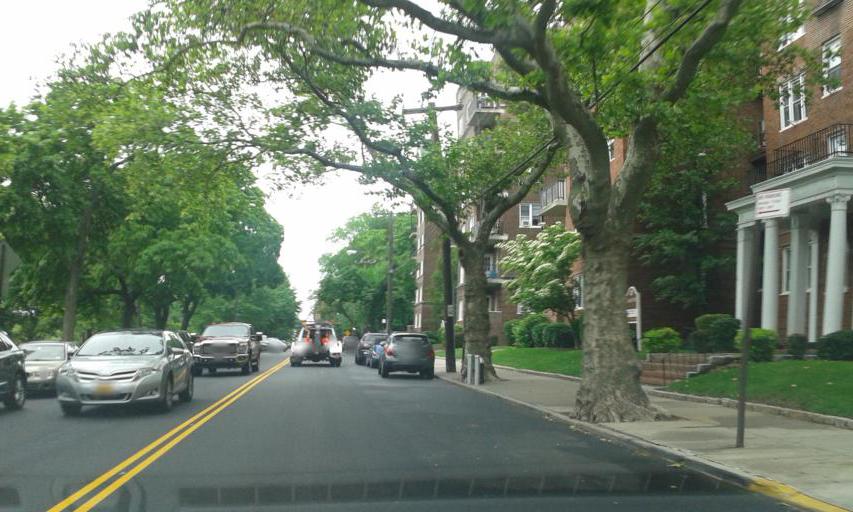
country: US
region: New Jersey
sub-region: Hudson County
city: Bayonne
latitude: 40.6269
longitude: -74.0913
